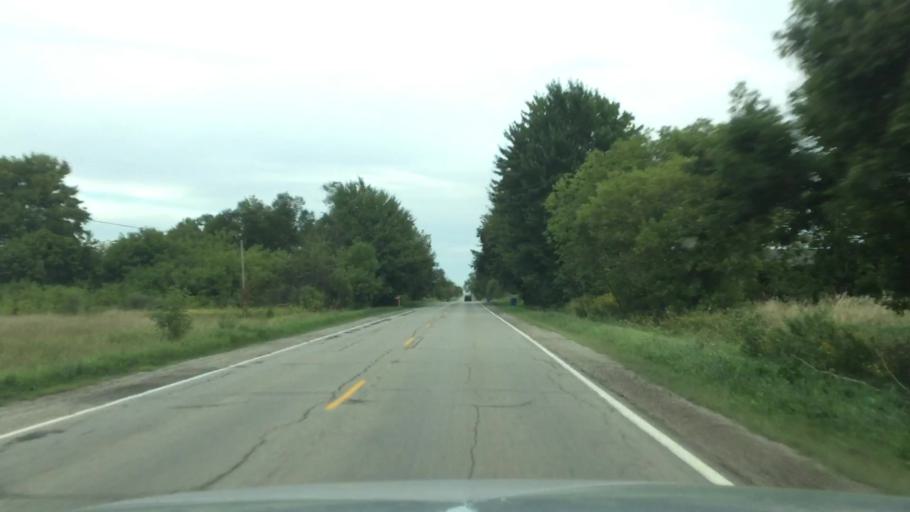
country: US
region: Michigan
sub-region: Genesee County
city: Lake Fenton
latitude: 42.8850
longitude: -83.7548
